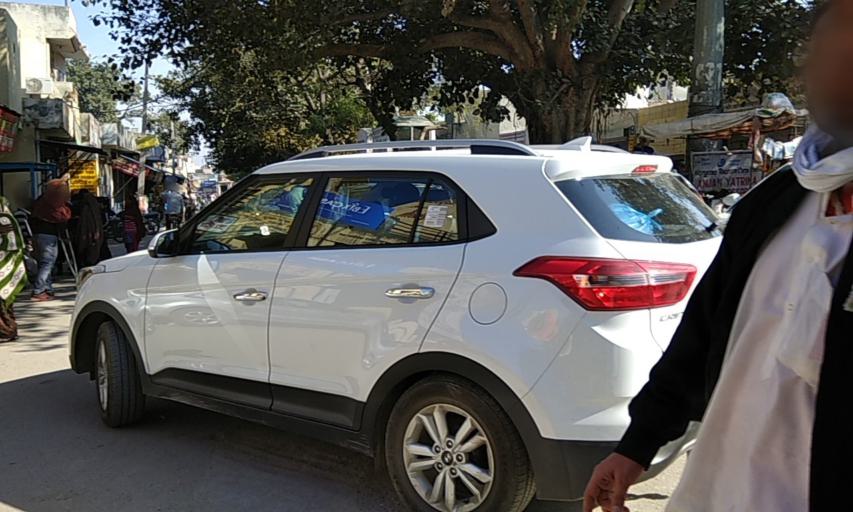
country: IN
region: Haryana
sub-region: Kurukshetra
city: Pehowa
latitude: 29.9817
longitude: 76.5797
